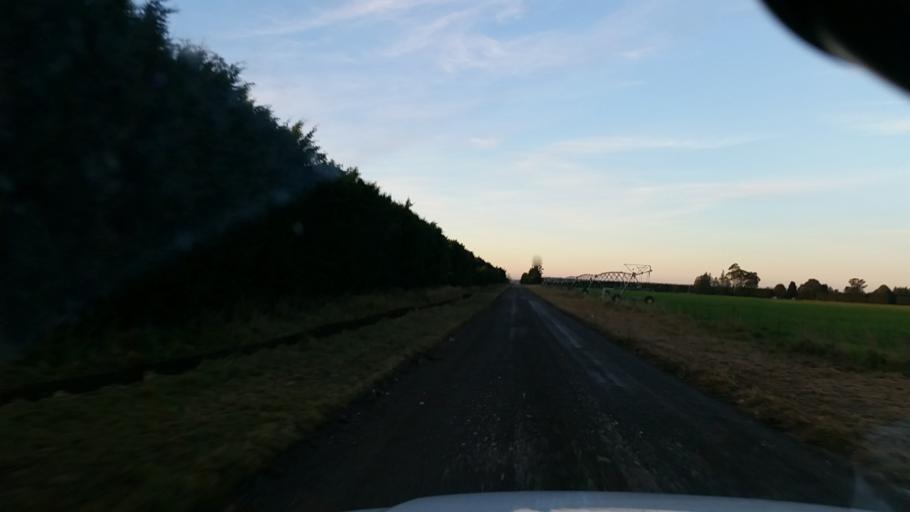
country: NZ
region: Canterbury
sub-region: Ashburton District
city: Methven
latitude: -43.7903
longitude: 171.5231
